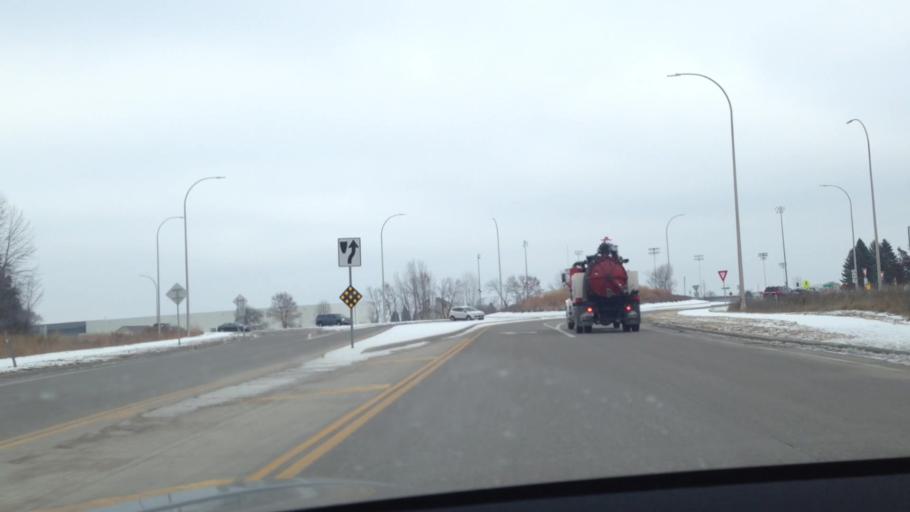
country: US
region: Minnesota
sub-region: Washington County
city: Forest Lake
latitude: 45.2549
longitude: -92.9855
